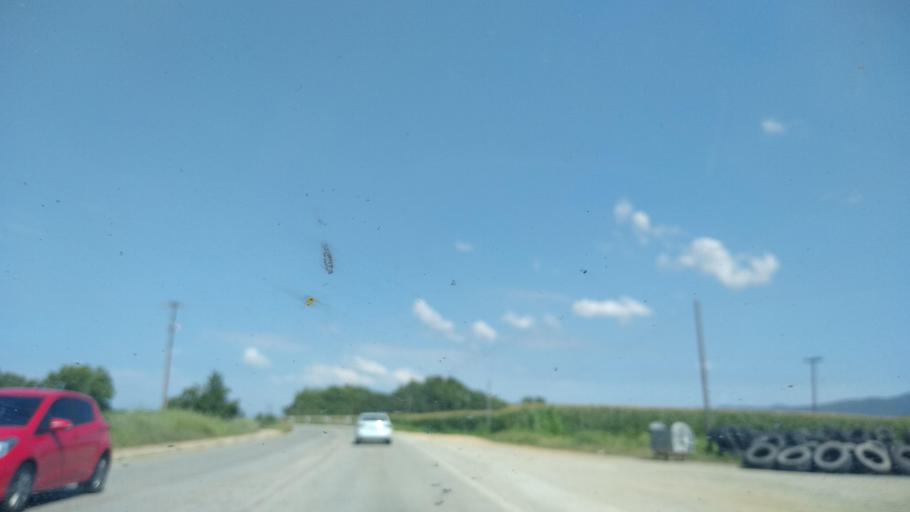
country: GR
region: Central Macedonia
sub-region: Nomos Thessalonikis
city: Nea Apollonia
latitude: 40.6365
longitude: 23.5008
